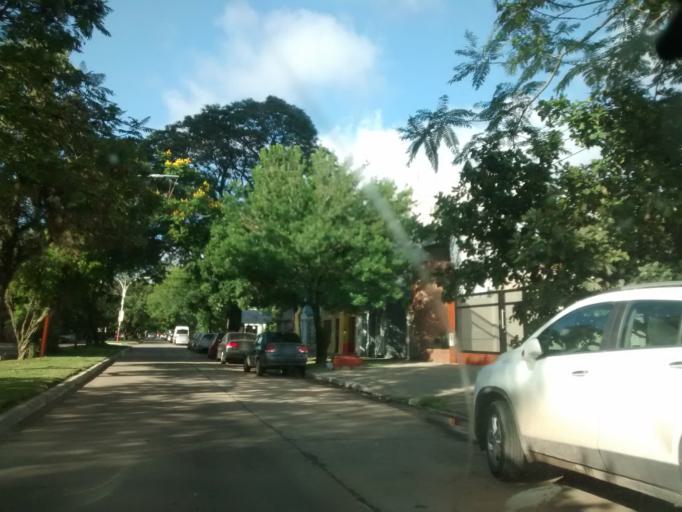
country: AR
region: Chaco
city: Resistencia
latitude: -27.4498
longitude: -58.9764
